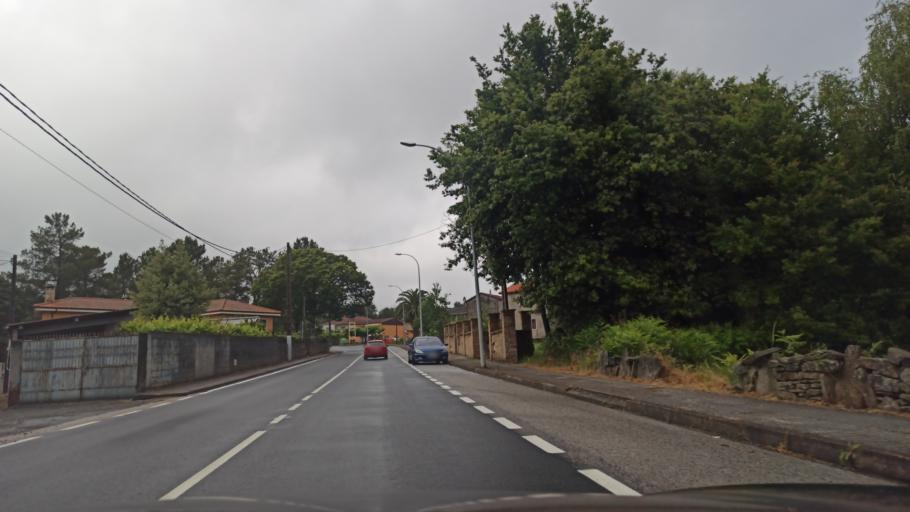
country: ES
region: Galicia
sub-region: Provincia da Coruna
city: Santiso
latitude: 42.7661
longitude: -8.0212
